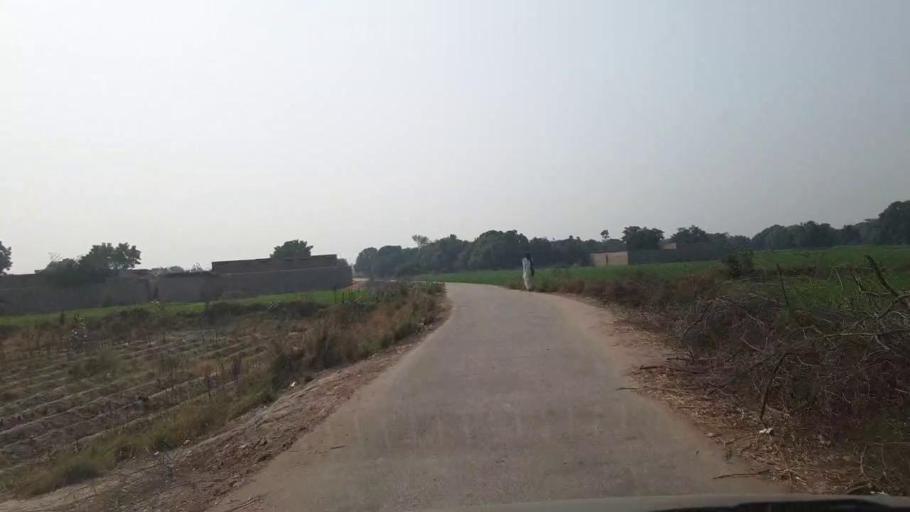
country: PK
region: Sindh
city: Bhit Shah
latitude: 25.8497
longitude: 68.5013
